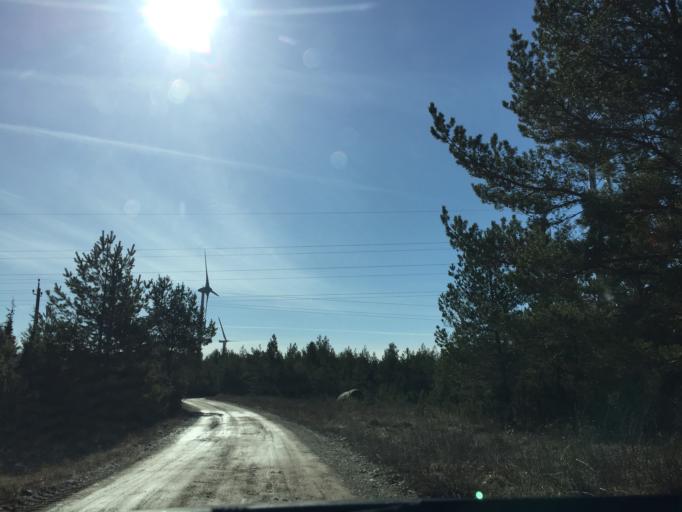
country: EE
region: Laeaene
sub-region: Haapsalu linn
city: Haapsalu
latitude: 58.6349
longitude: 23.5240
